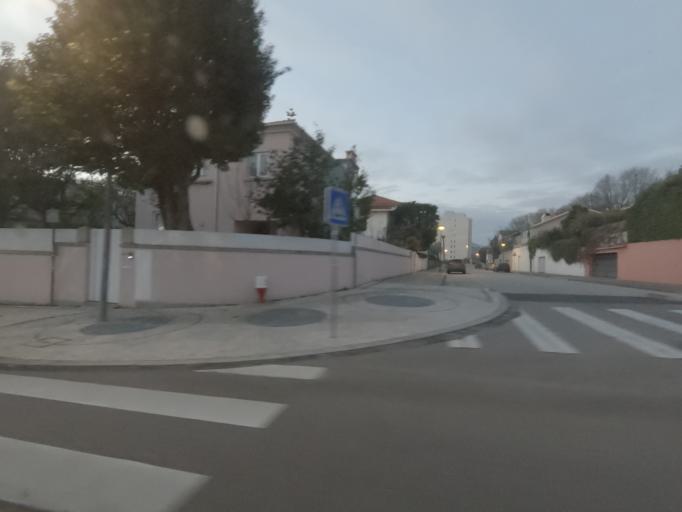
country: PT
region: Porto
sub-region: Matosinhos
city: Matosinhos
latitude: 41.1573
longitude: -8.6696
